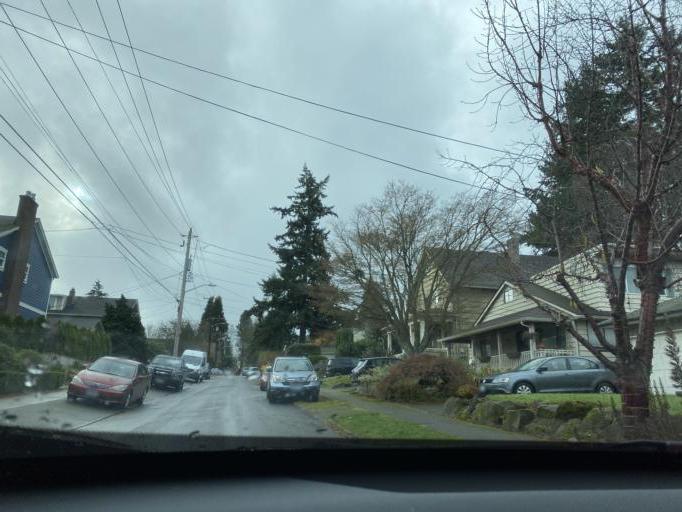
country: US
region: Washington
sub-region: King County
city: Seattle
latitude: 47.6633
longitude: -122.4025
